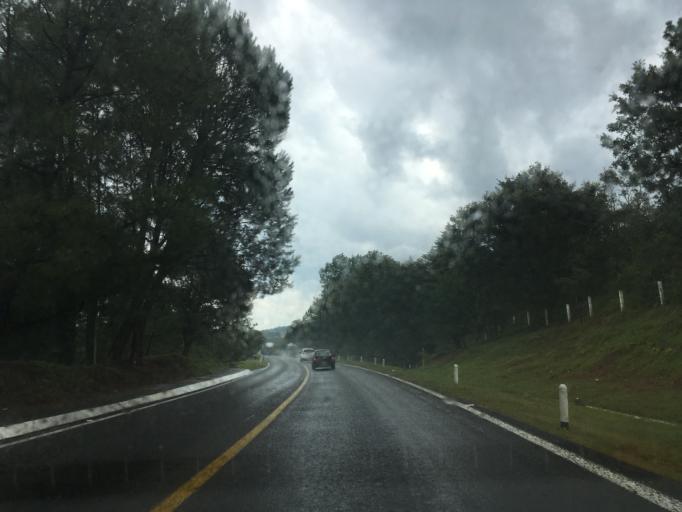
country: MX
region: Michoacan
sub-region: Patzcuaro
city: Santa Ana Chapitiro
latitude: 19.5073
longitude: -101.6893
